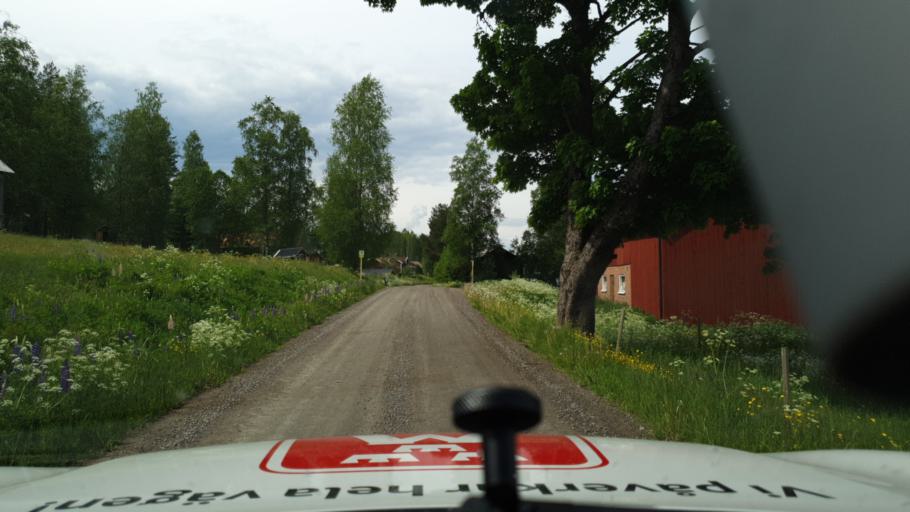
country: SE
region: Vaermland
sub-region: Torsby Kommun
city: Torsby
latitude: 59.9701
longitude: 12.8678
